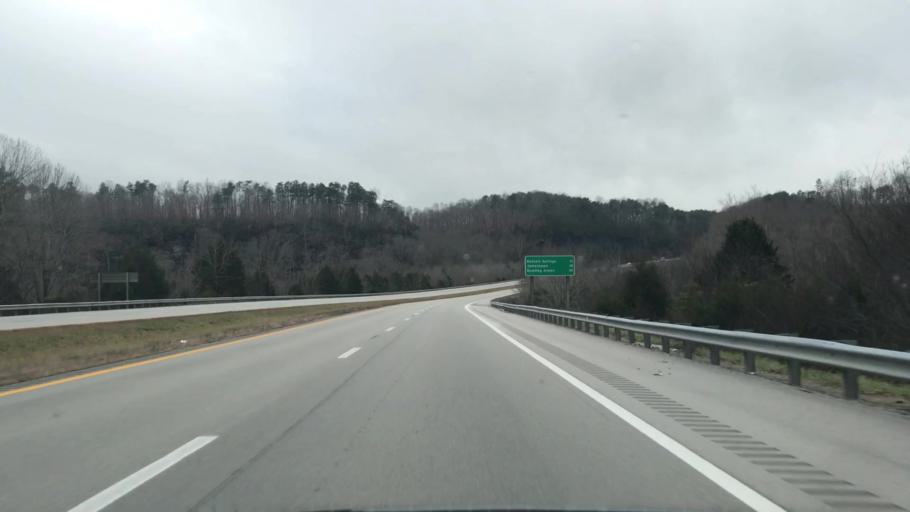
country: US
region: Kentucky
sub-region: Russell County
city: Russell Springs
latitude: 37.0895
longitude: -84.8845
